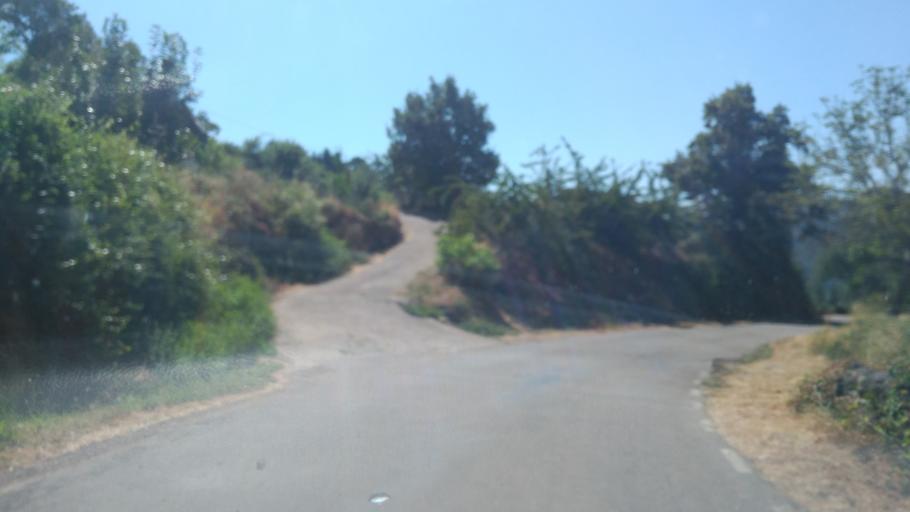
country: ES
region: Castille and Leon
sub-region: Provincia de Salamanca
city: San Martin del Castanar
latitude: 40.5261
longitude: -6.0662
